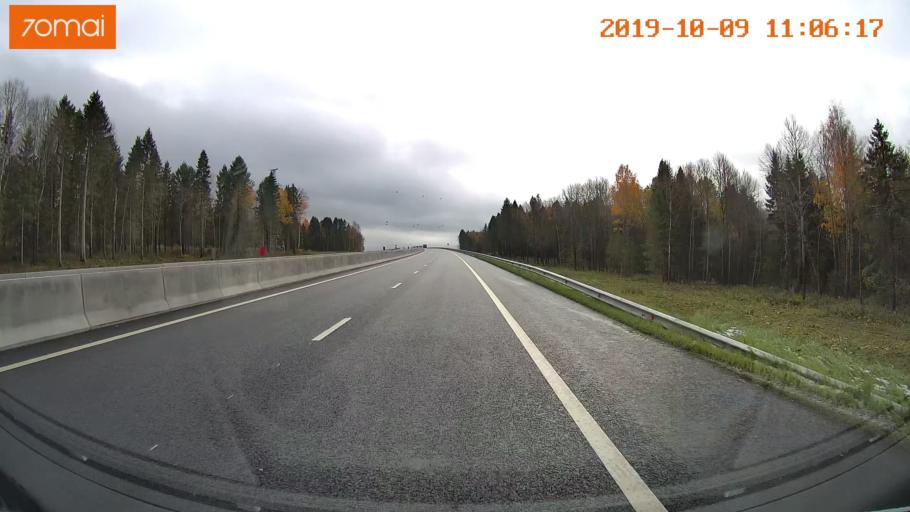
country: RU
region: Vologda
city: Vologda
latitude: 59.1885
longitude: 39.7595
